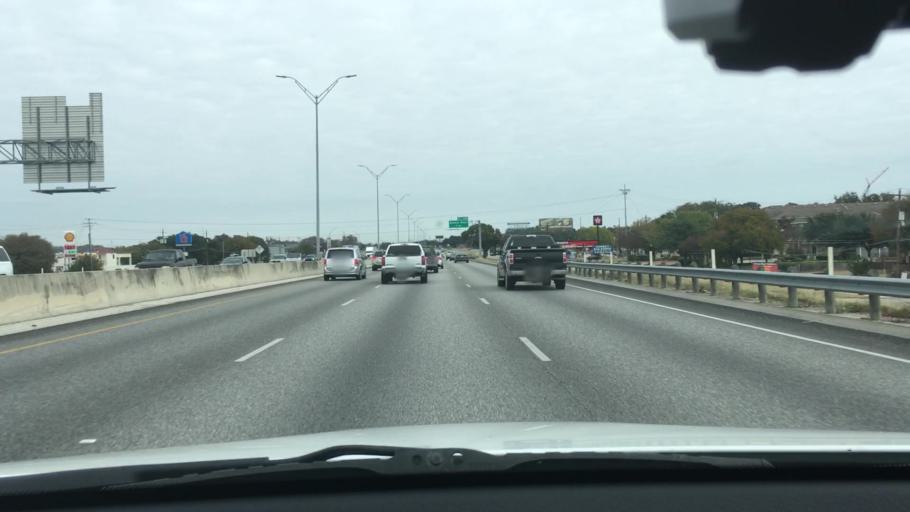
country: US
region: Texas
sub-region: Hays County
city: San Marcos
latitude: 29.8945
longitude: -97.9110
